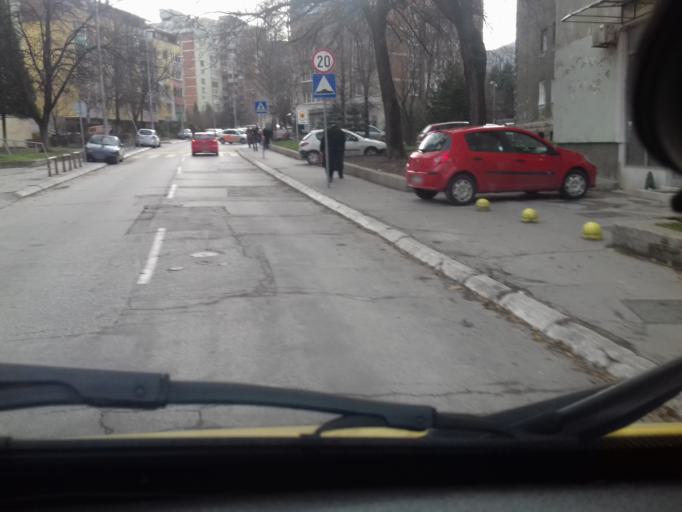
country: BA
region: Federation of Bosnia and Herzegovina
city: Zenica
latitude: 44.1949
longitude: 17.9106
